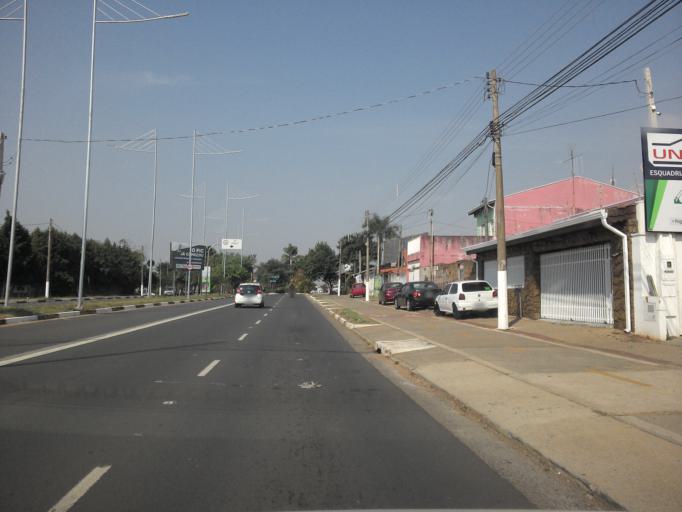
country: BR
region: Sao Paulo
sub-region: Hortolandia
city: Hortolandia
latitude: -22.8767
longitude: -47.2024
